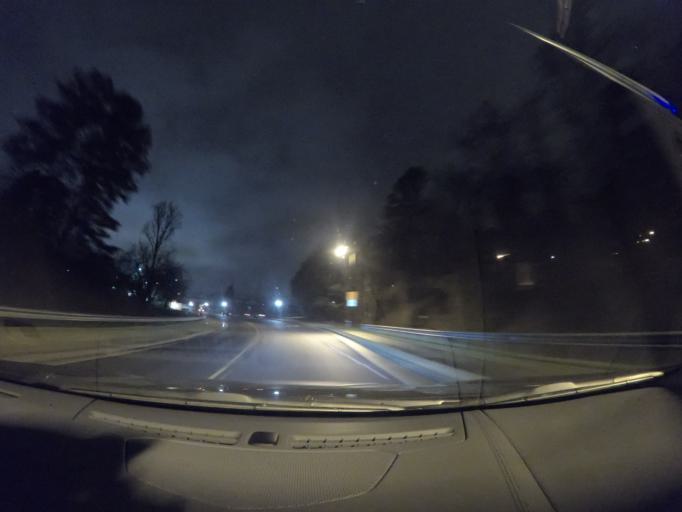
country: US
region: Georgia
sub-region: Cobb County
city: Acworth
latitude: 34.0665
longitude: -84.6673
